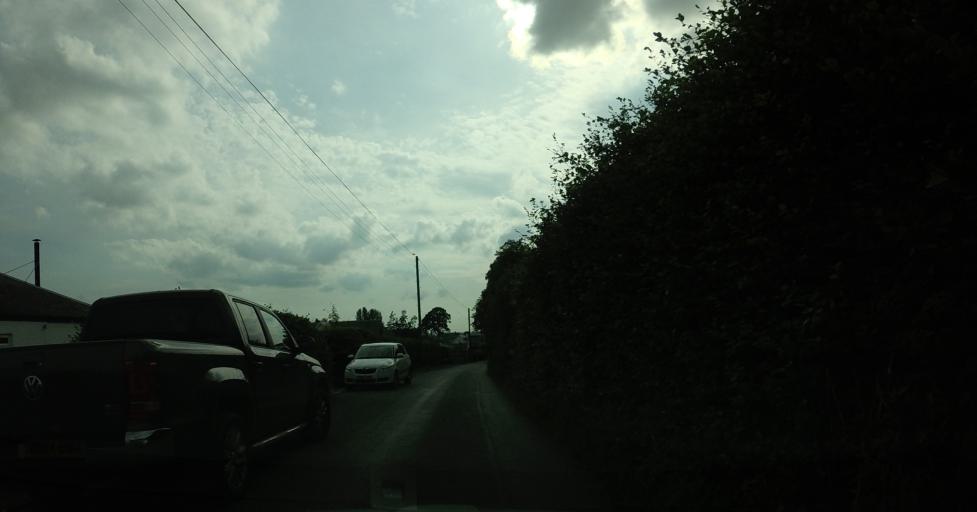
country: GB
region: Scotland
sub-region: Perth and Kinross
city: Auchterarder
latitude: 56.3621
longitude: -3.7004
